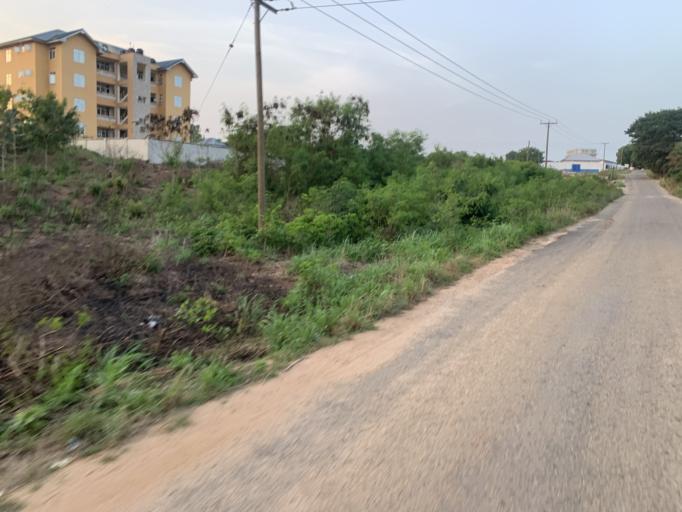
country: GH
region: Central
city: Winneba
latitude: 5.3651
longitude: -0.6201
